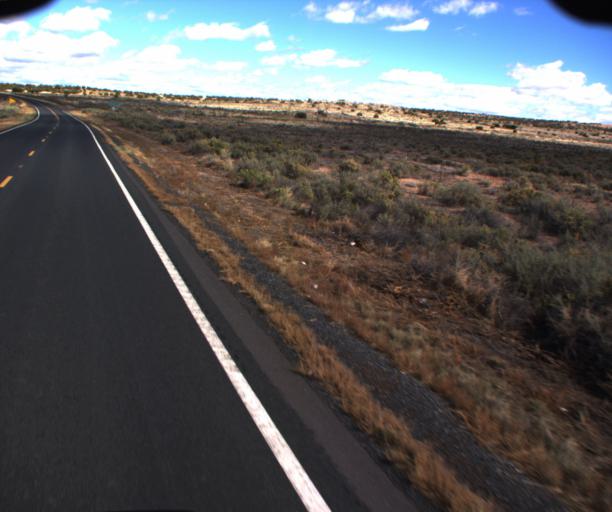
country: US
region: Arizona
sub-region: Apache County
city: Houck
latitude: 35.0954
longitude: -109.3122
